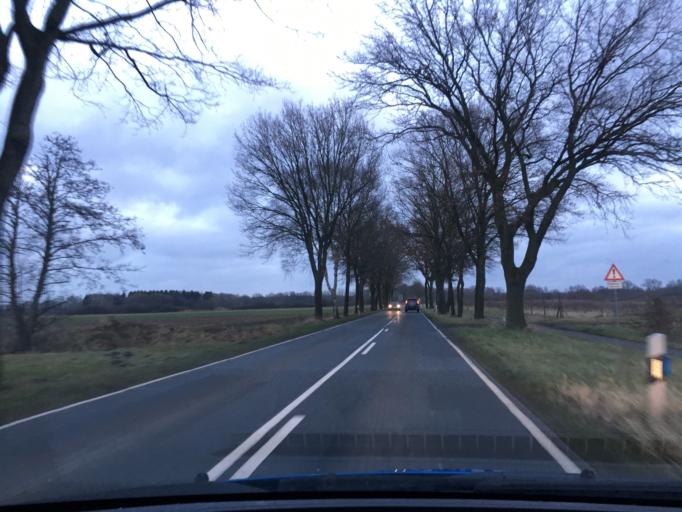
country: DE
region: Lower Saxony
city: Winsen
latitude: 53.3268
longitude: 10.2158
